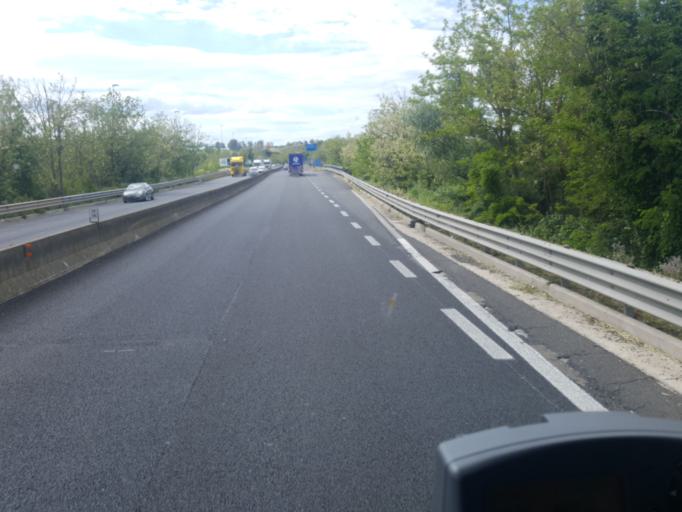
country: IT
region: Latium
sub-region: Citta metropolitana di Roma Capitale
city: La Massimina-Casal Lumbroso
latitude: 41.8834
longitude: 12.3388
